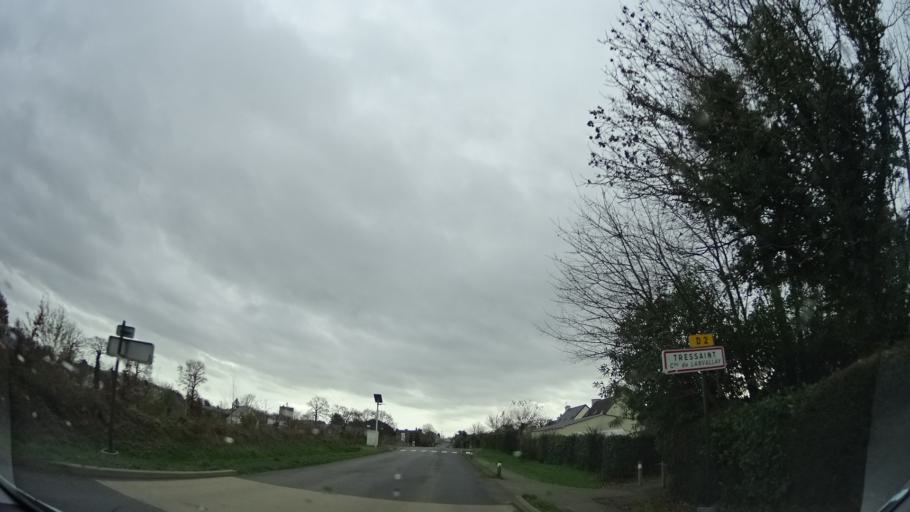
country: FR
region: Brittany
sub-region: Departement des Cotes-d'Armor
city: Lanvallay
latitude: 48.4391
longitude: -2.0162
